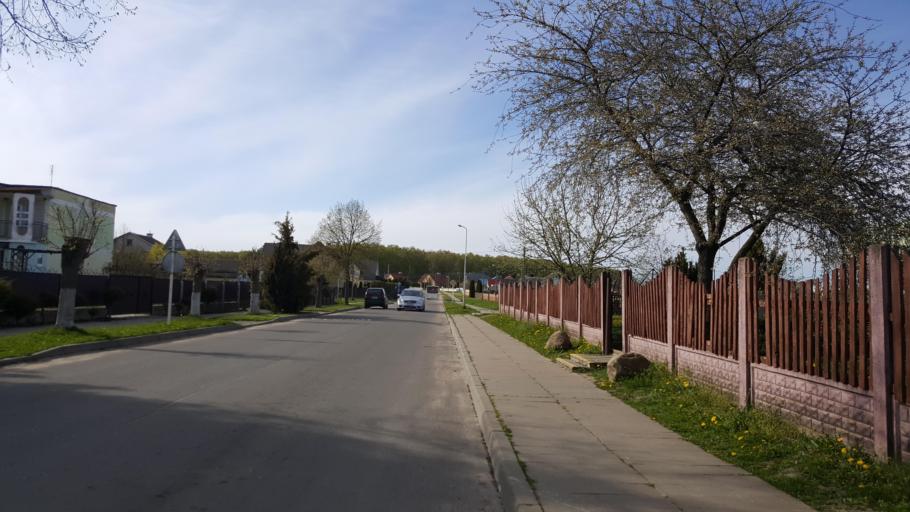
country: BY
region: Brest
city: Vysokaye
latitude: 52.4040
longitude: 23.4633
